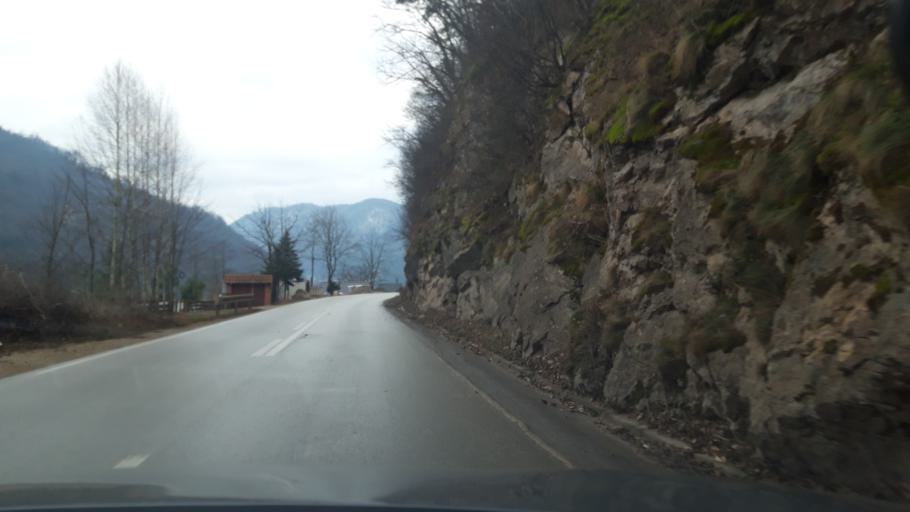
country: RS
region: Central Serbia
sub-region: Macvanski Okrug
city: Mali Zvornik
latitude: 44.3506
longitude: 19.1093
